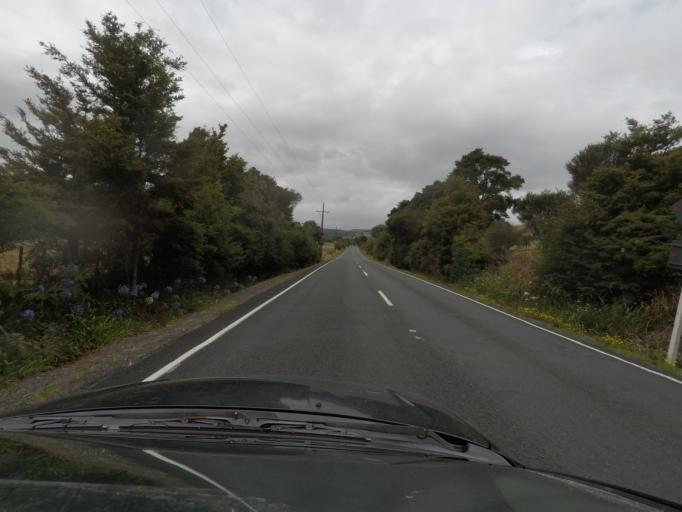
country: NZ
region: Auckland
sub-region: Auckland
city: Wellsford
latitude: -36.2931
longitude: 174.6223
